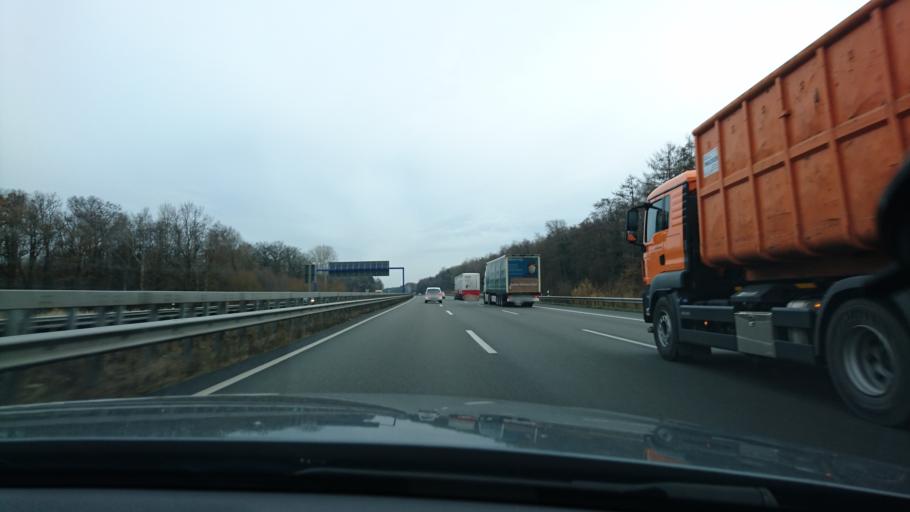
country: DE
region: Lower Saxony
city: Wallenhorst
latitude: 52.3537
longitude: 8.0340
